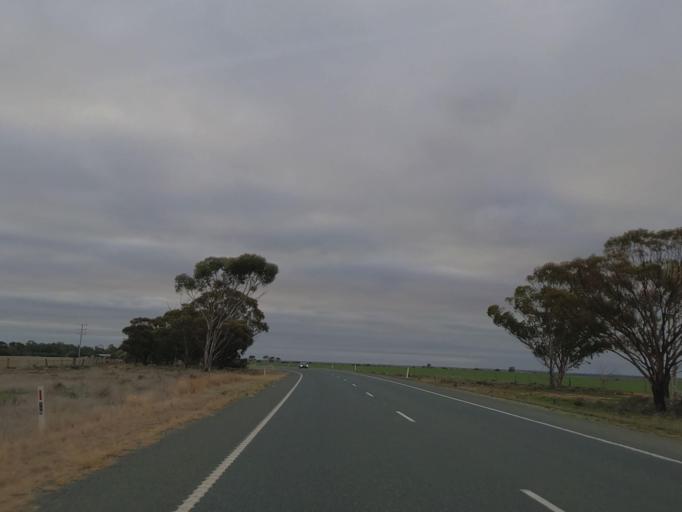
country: AU
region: Victoria
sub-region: Swan Hill
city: Swan Hill
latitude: -35.5636
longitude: 143.7830
